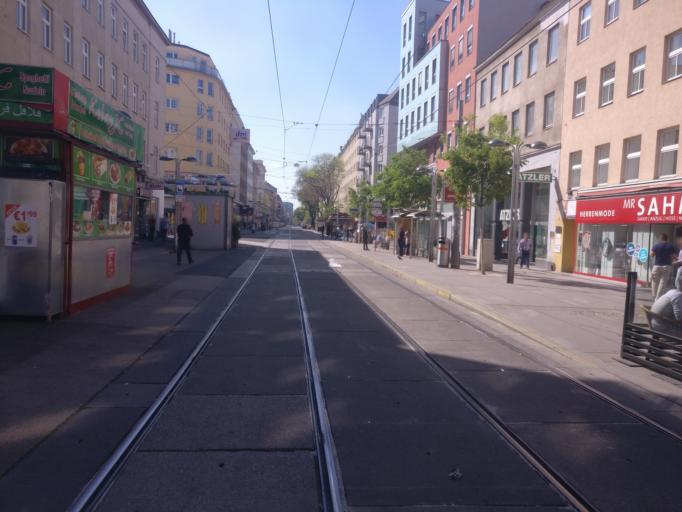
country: AT
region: Vienna
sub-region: Wien Stadt
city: Vienna
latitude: 48.1753
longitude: 16.3785
